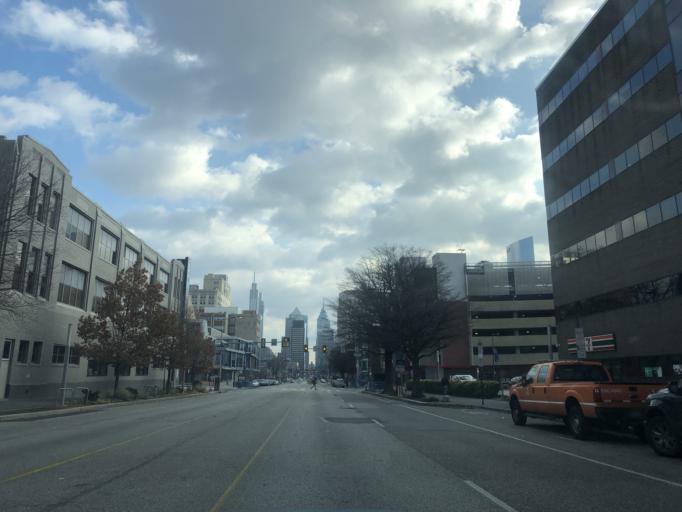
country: US
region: Pennsylvania
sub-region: Philadelphia County
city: Philadelphia
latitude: 39.9559
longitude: -75.1925
